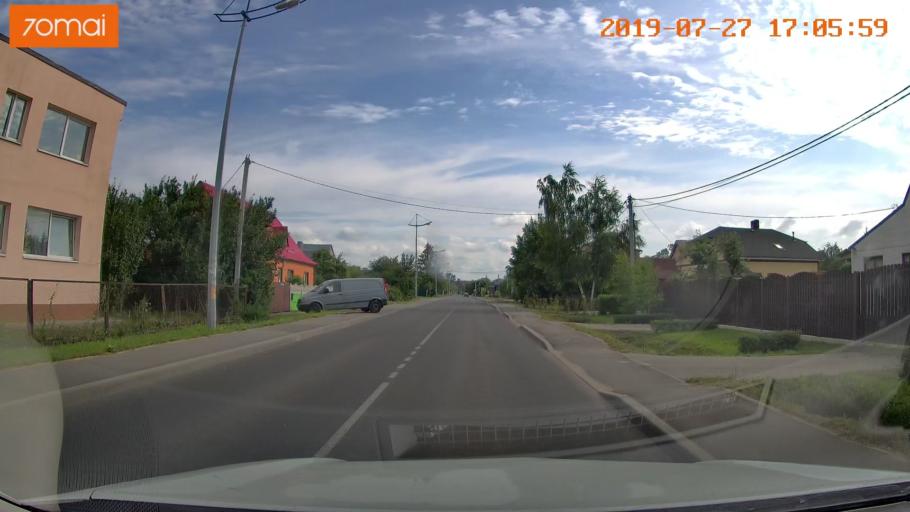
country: RU
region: Kaliningrad
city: Bol'shoe Isakovo
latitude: 54.7244
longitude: 20.6013
